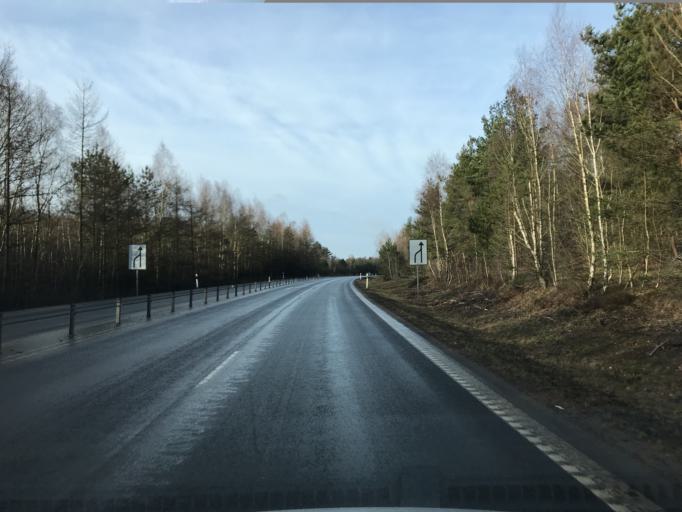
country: SE
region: Skane
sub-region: Hassleholms Kommun
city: Hassleholm
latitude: 56.1771
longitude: 13.7191
